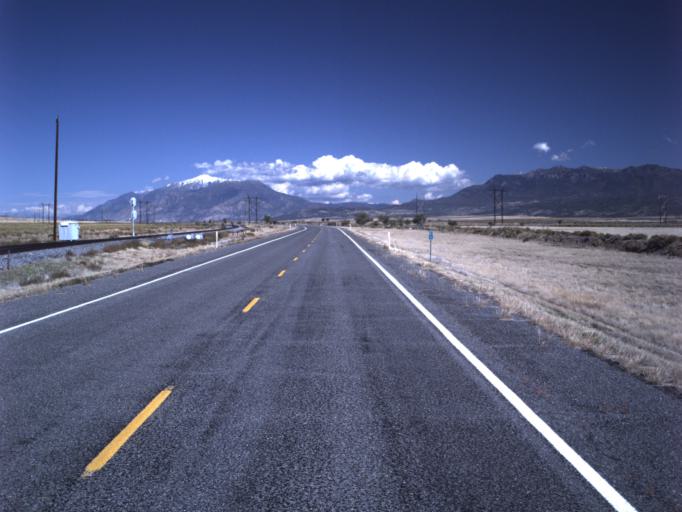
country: US
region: Utah
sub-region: Juab County
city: Nephi
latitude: 39.5236
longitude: -111.9371
